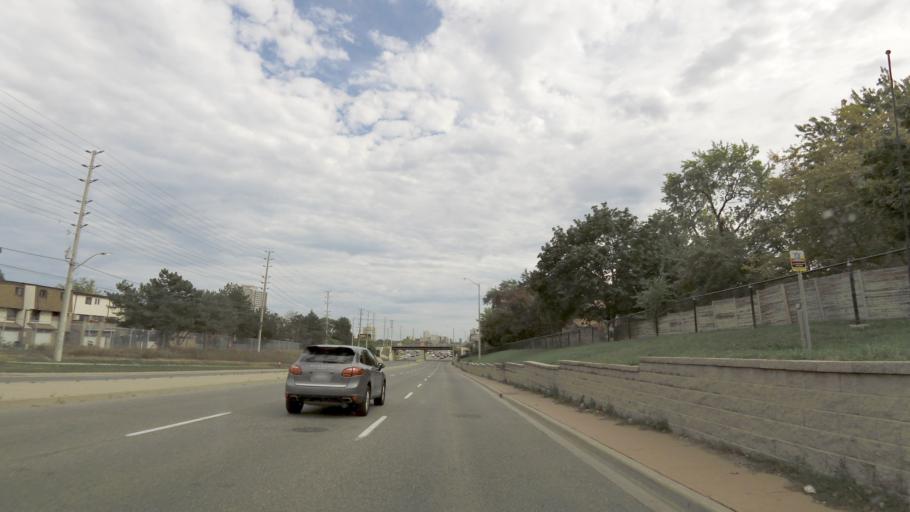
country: CA
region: Ontario
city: Mississauga
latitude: 43.5857
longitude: -79.6244
